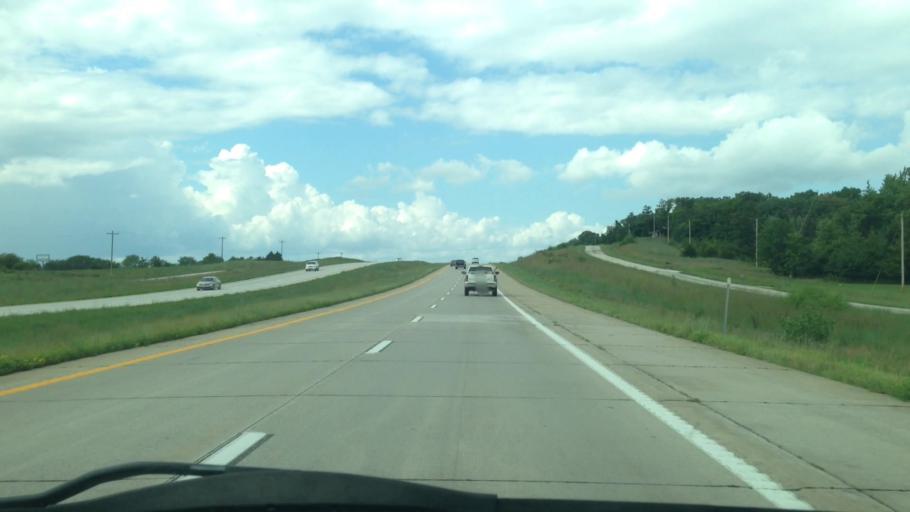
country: US
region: Missouri
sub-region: Pike County
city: Bowling Green
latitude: 39.4307
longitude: -91.2567
